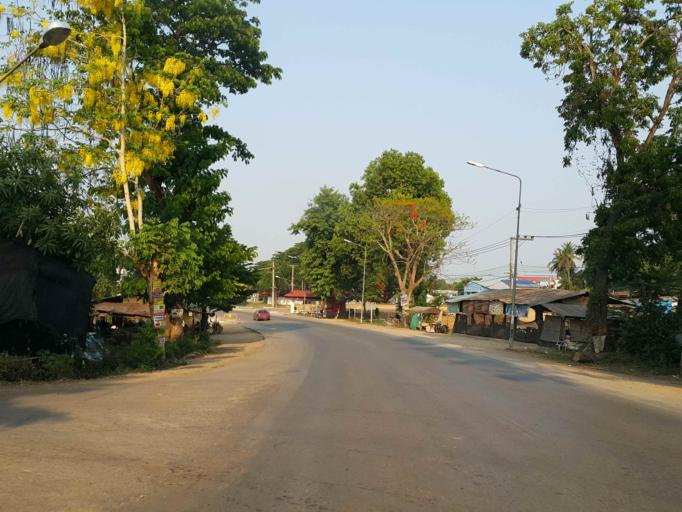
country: TH
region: Sukhothai
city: Sawankhalok
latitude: 17.3024
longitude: 99.8316
